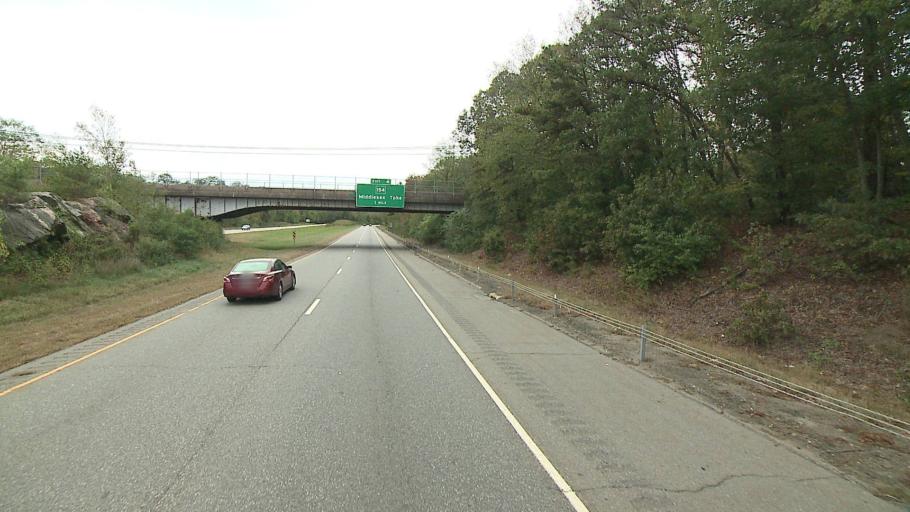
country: US
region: Connecticut
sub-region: Middlesex County
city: Essex Village
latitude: 41.3542
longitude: -72.4076
